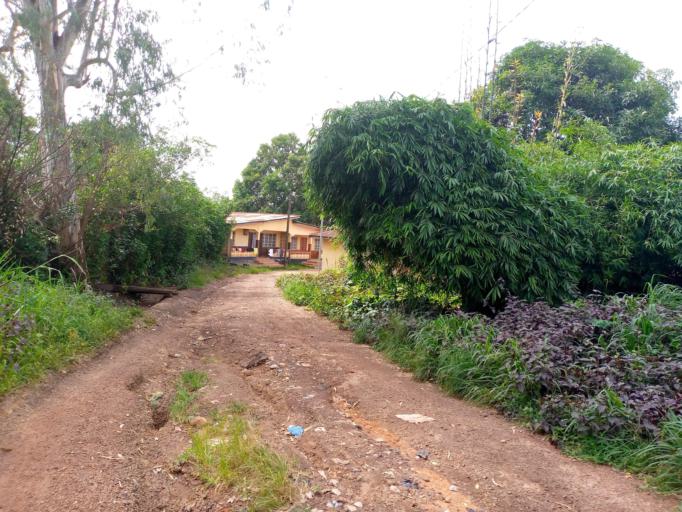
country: SL
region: Northern Province
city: Magburaka
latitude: 8.7226
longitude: -11.9401
